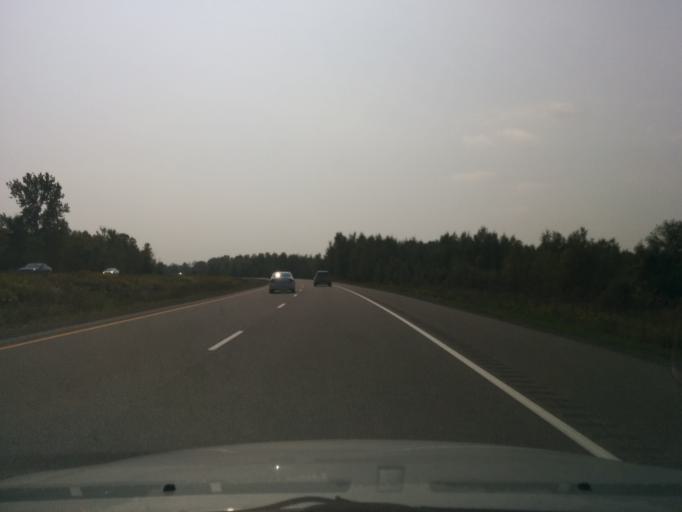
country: CA
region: Ontario
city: Bells Corners
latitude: 45.1186
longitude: -75.6759
